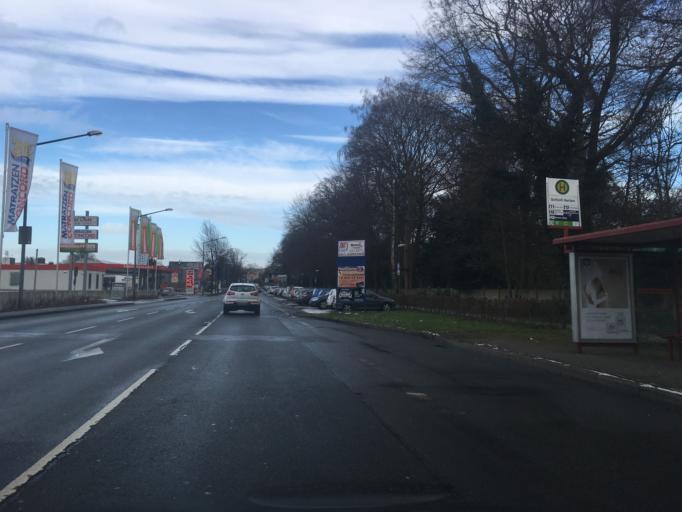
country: DE
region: North Rhine-Westphalia
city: Herten
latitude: 51.5943
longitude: 7.1276
